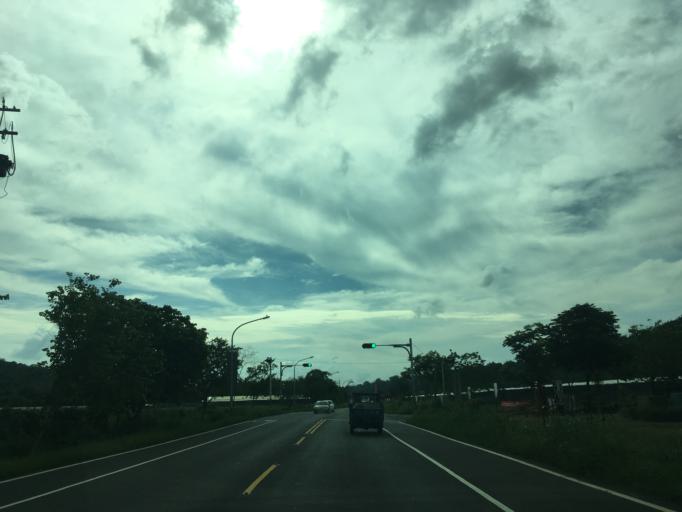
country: TW
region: Taiwan
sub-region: Chiayi
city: Jiayi Shi
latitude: 23.4467
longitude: 120.5814
